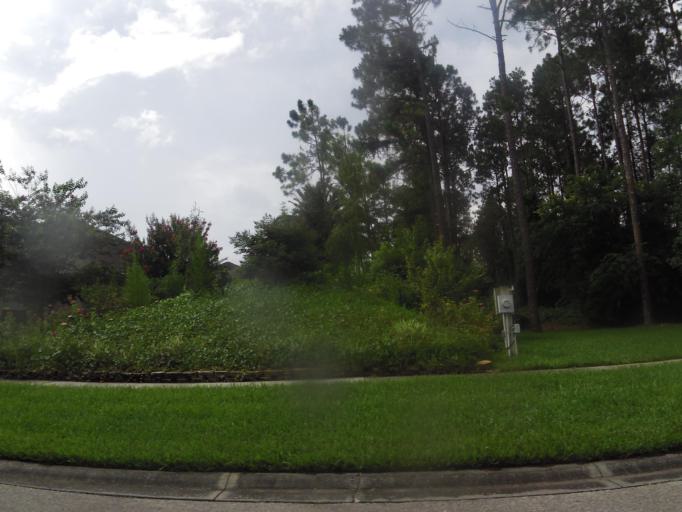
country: US
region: Florida
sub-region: Duval County
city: Jacksonville Beach
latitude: 30.2620
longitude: -81.4552
